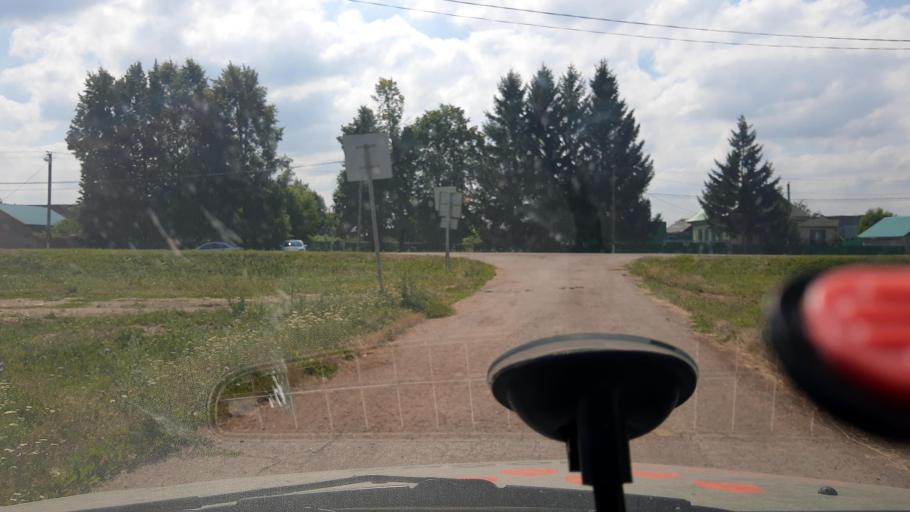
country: RU
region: Bashkortostan
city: Chekmagush
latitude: 54.8768
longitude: 54.6126
